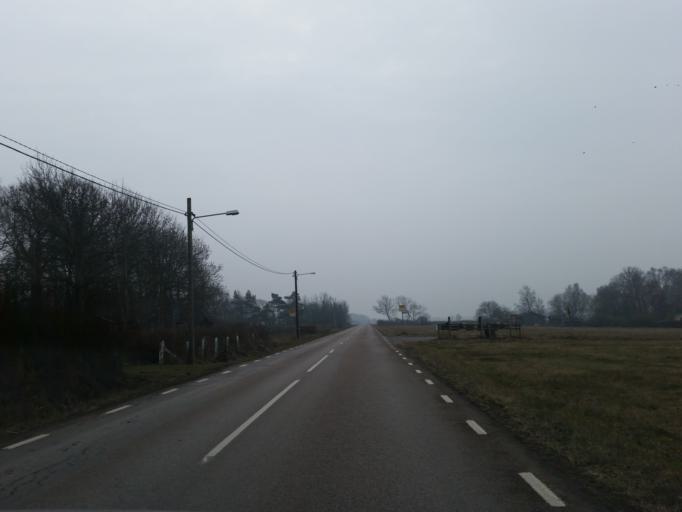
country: SE
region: Kalmar
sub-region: Morbylanga Kommun
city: Moerbylanga
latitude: 56.4179
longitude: 16.4135
